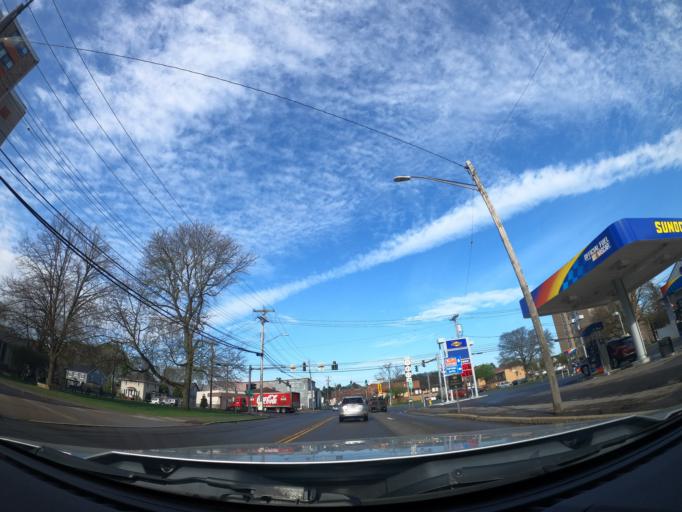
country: US
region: New York
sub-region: Cortland County
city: Cortland
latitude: 42.5978
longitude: -76.1772
